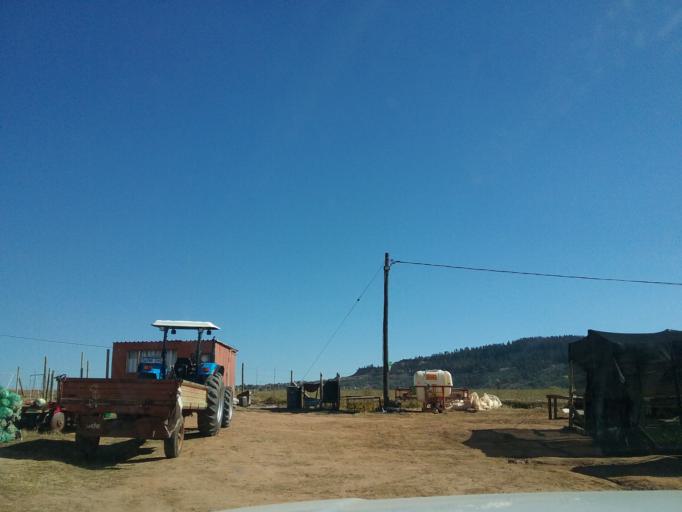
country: LS
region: Maseru
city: Nako
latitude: -29.4951
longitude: 27.5966
